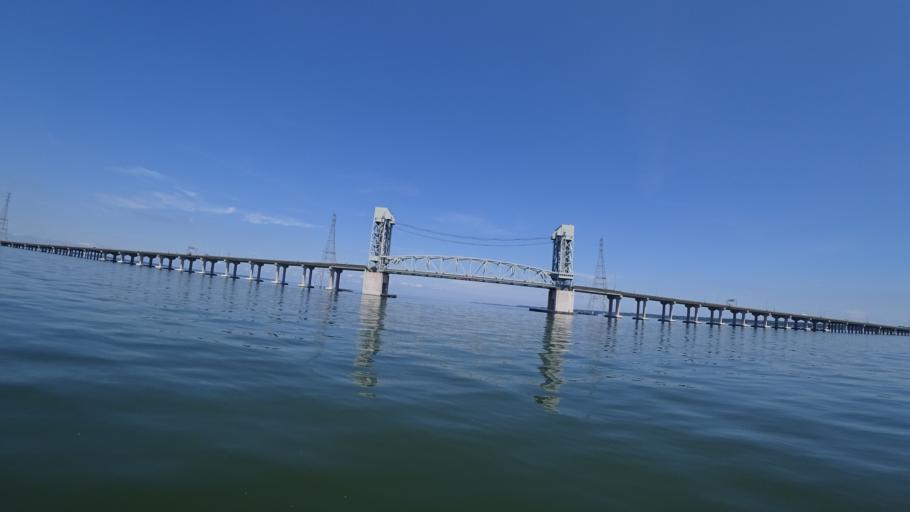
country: US
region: Virginia
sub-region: City of Newport News
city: Newport News
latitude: 37.0010
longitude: -76.4665
